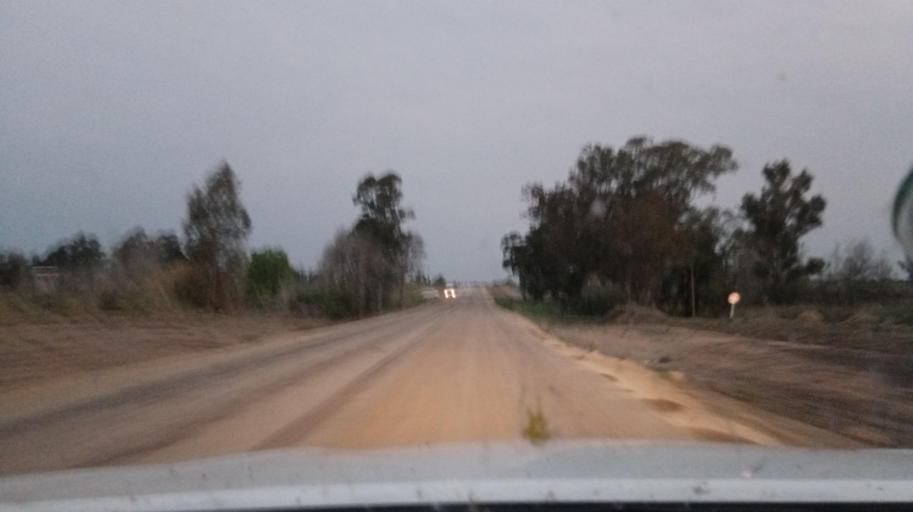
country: UY
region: Canelones
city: Santa Rosa
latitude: -34.5603
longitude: -56.1025
